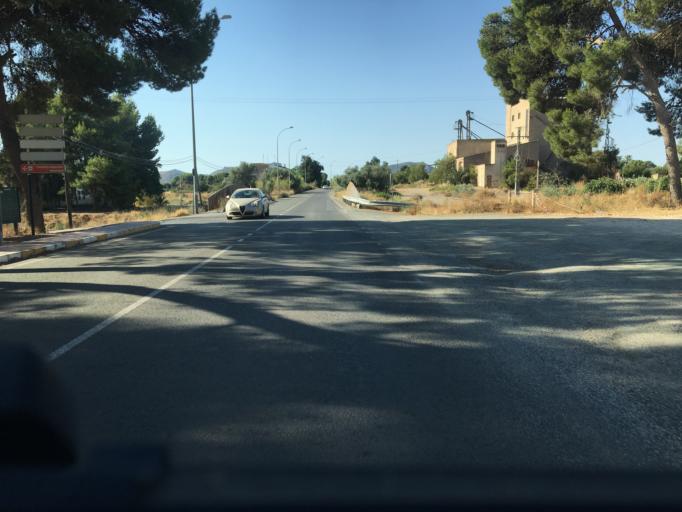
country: ES
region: Murcia
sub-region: Murcia
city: Puerto Lumbreras
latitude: 37.5457
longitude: -1.8145
